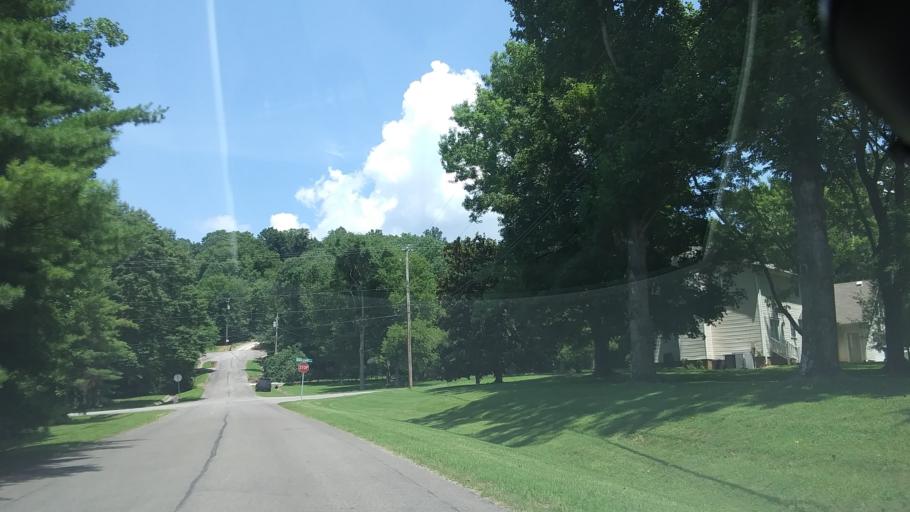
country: US
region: Tennessee
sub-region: Davidson County
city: Belle Meade
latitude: 36.0889
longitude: -86.9480
